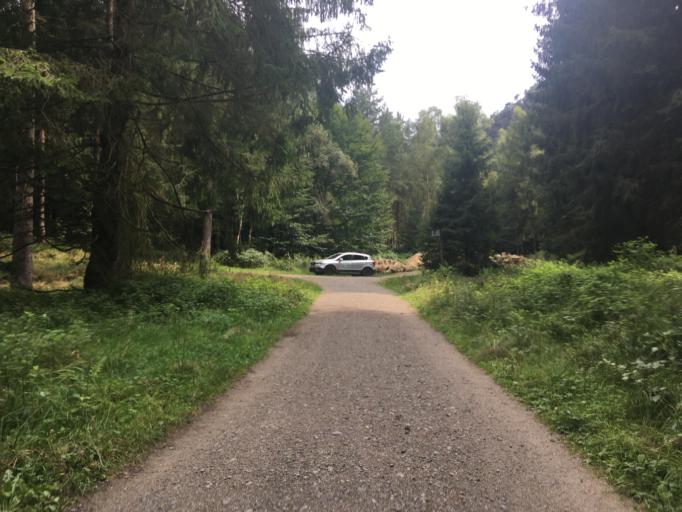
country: DE
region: Saxony
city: Bad Schandau
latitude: 50.9116
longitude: 14.2140
